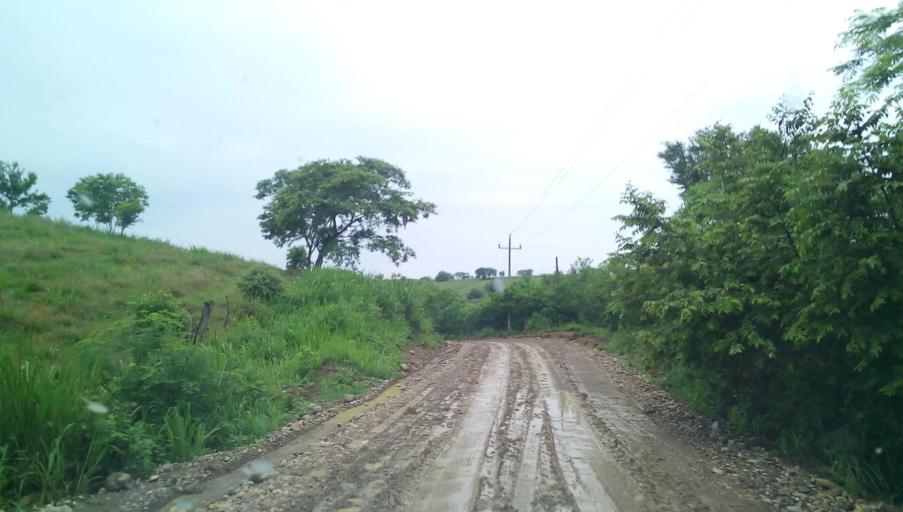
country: MX
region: Veracruz
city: Tempoal de Sanchez
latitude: 21.4493
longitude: -98.4241
